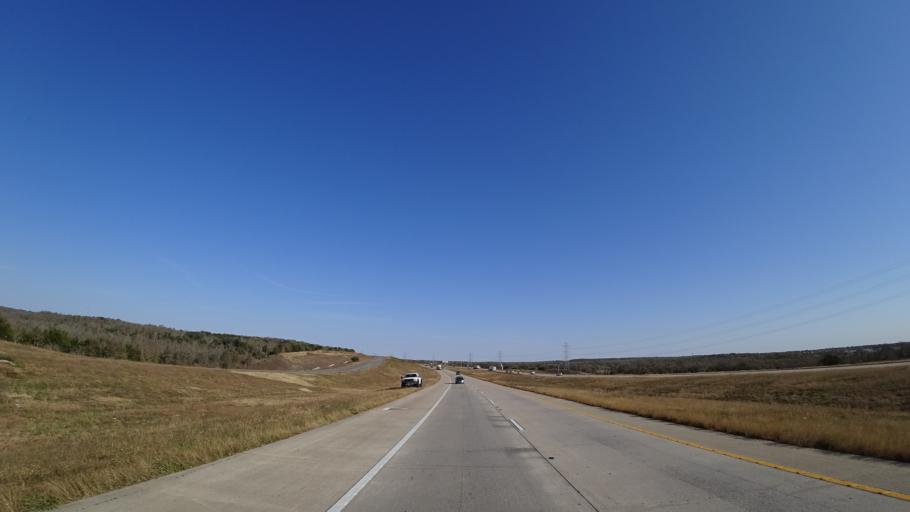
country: US
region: Texas
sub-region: Travis County
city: Manor
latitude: 30.2947
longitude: -97.5717
